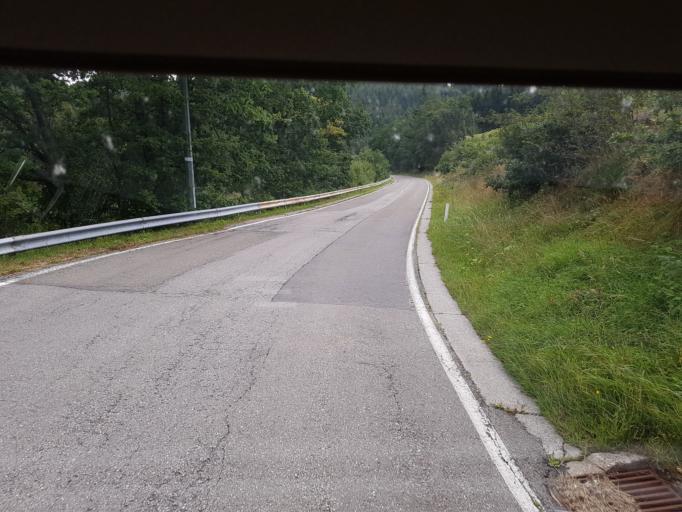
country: DE
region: Rheinland-Pfalz
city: Winterspelt
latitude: 50.2479
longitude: 6.1765
